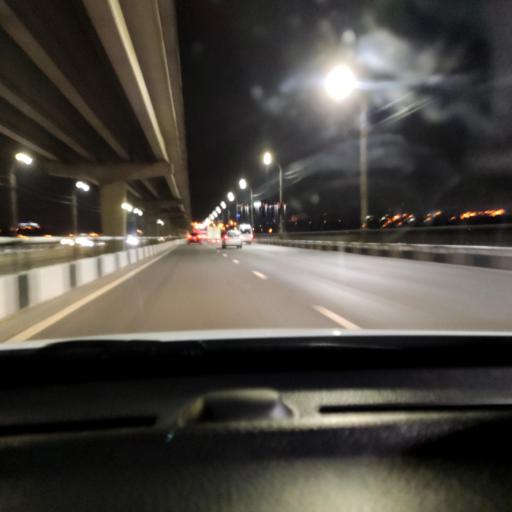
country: RU
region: Voronezj
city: Voronezh
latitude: 51.6906
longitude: 39.2456
